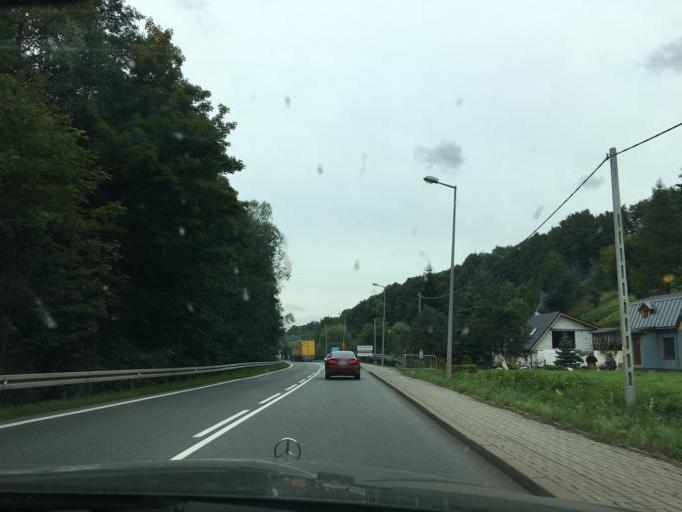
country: PL
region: Lower Silesian Voivodeship
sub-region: Powiat klodzki
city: Lewin Klodzki
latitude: 50.4151
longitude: 16.2654
